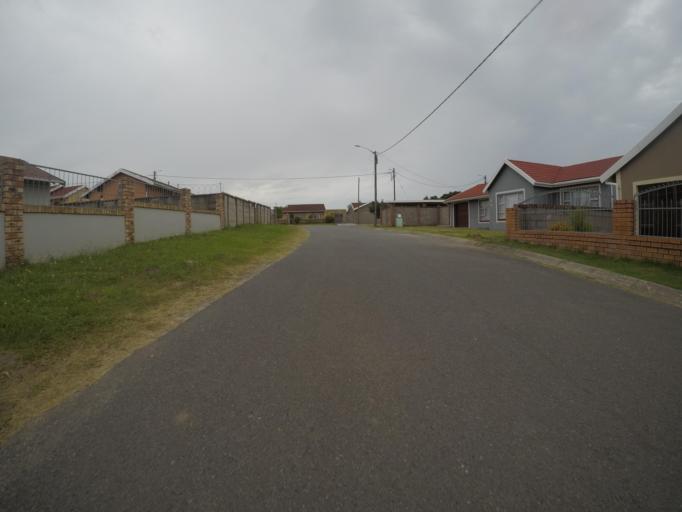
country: ZA
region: Eastern Cape
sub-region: Buffalo City Metropolitan Municipality
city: East London
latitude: -32.9965
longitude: 27.8459
